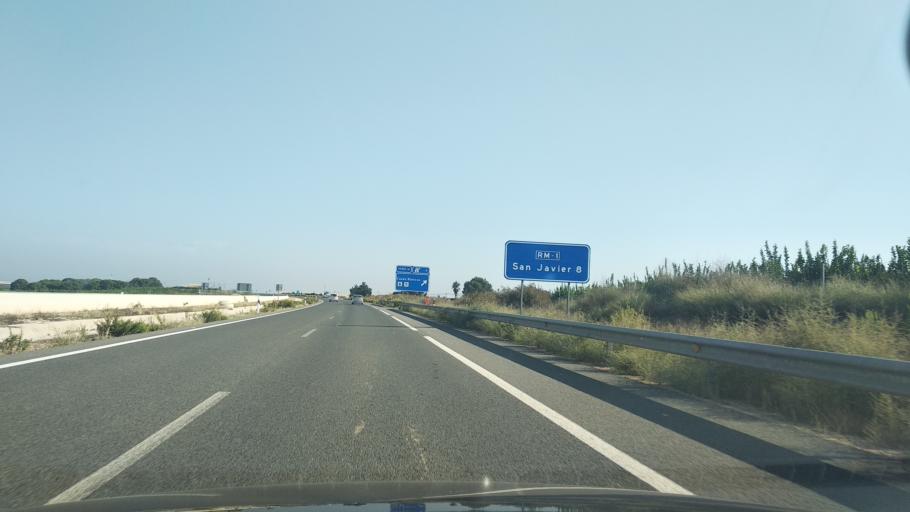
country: ES
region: Murcia
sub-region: Murcia
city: San Javier
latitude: 37.8589
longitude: -0.8891
